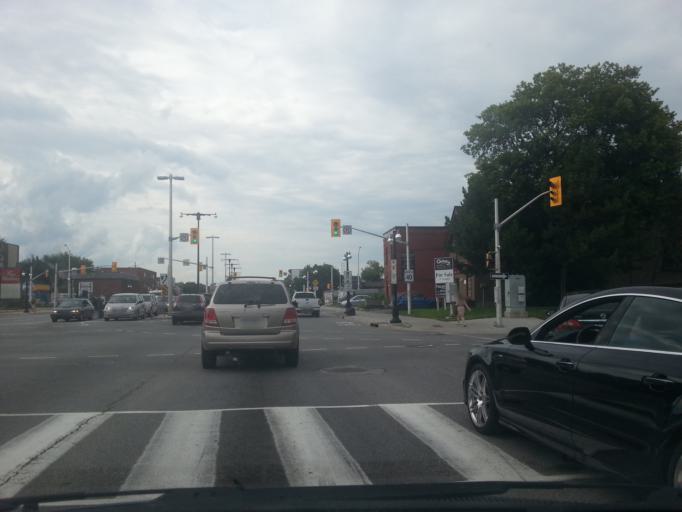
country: CA
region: Ontario
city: Ottawa
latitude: 45.4319
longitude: -75.6883
